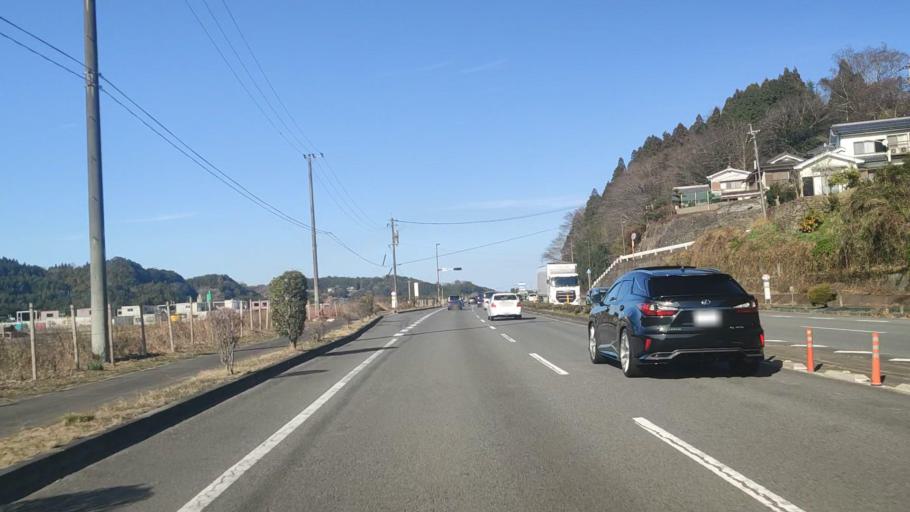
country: JP
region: Oita
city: Oita
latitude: 33.1187
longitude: 131.6536
